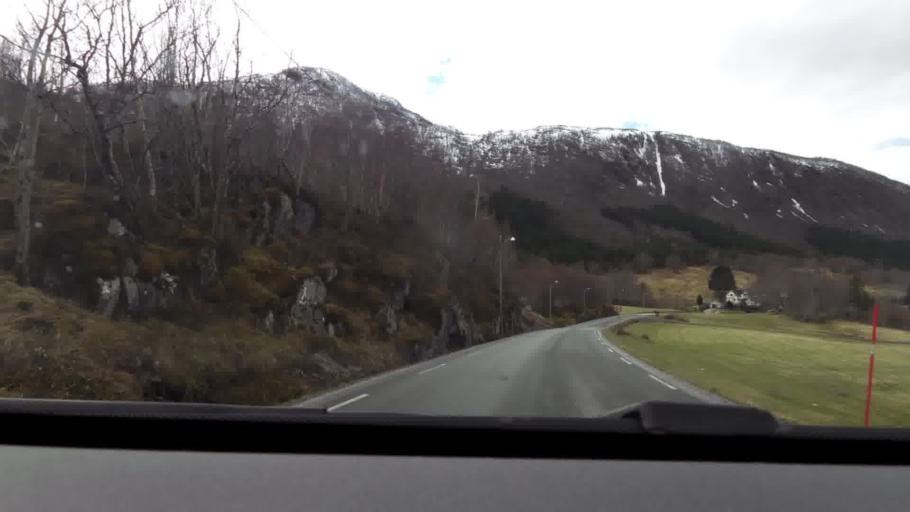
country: NO
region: More og Romsdal
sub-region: Kristiansund
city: Rensvik
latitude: 63.1108
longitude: 7.8032
